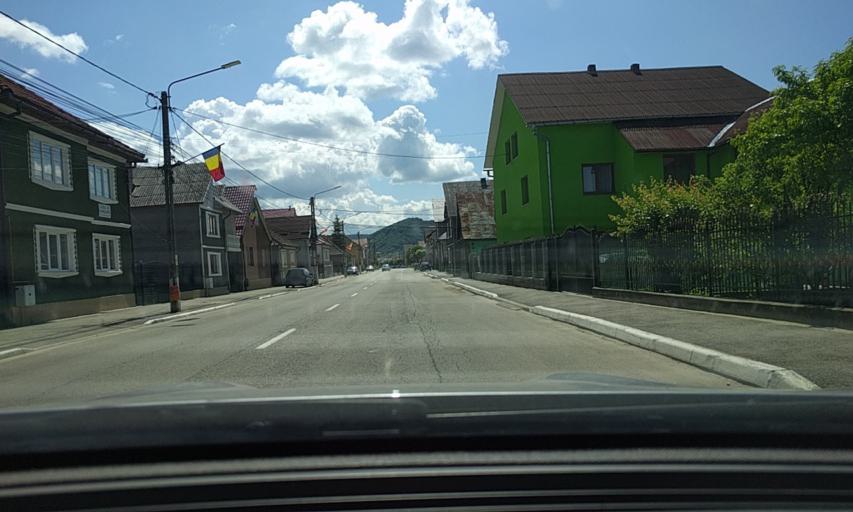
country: RO
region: Bistrita-Nasaud
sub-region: Oras Nasaud
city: Nasaud
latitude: 47.2905
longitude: 24.3903
